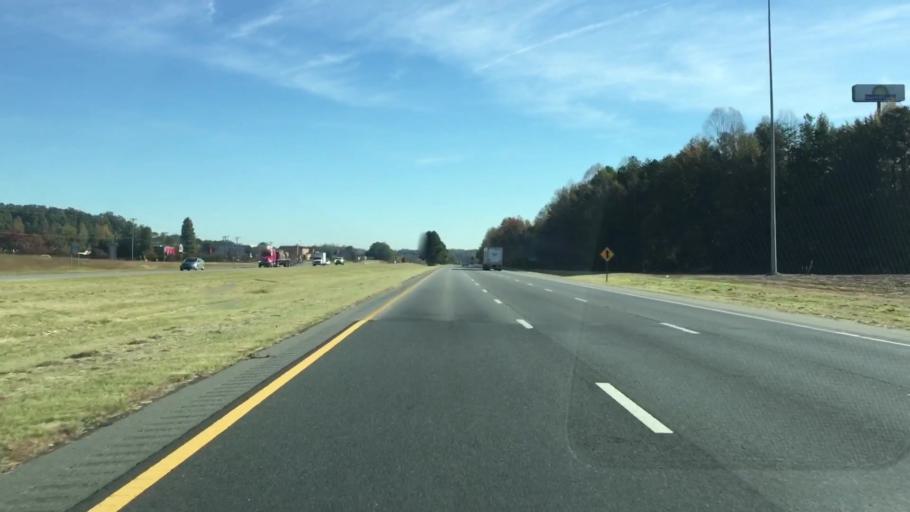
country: US
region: North Carolina
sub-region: Davidson County
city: Lexington
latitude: 35.7808
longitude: -80.2582
